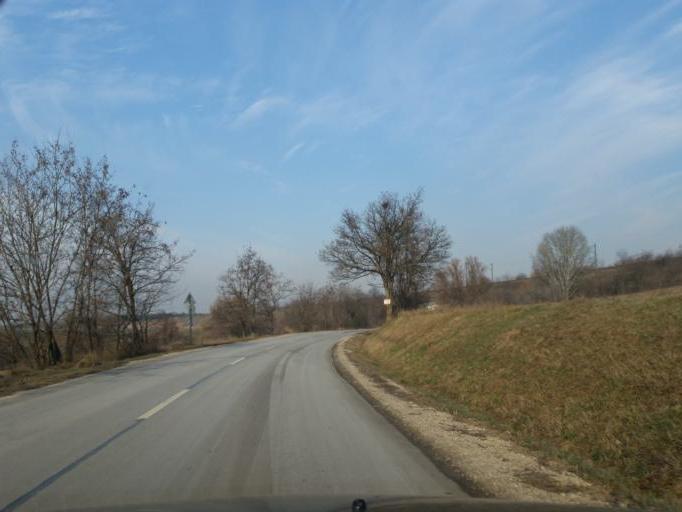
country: HU
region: Pest
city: Biatorbagy
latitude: 47.4854
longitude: 18.8268
